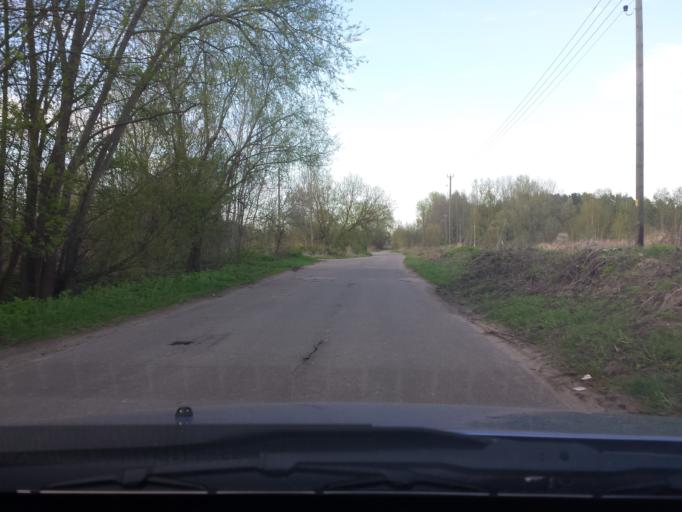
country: LV
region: Riga
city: Jaunciems
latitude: 56.9943
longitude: 24.2162
